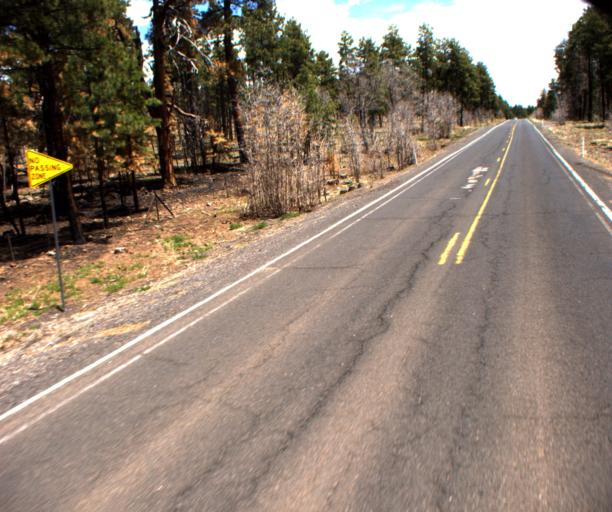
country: US
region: Arizona
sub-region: Coconino County
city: Kachina Village
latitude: 35.1047
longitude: -111.7264
